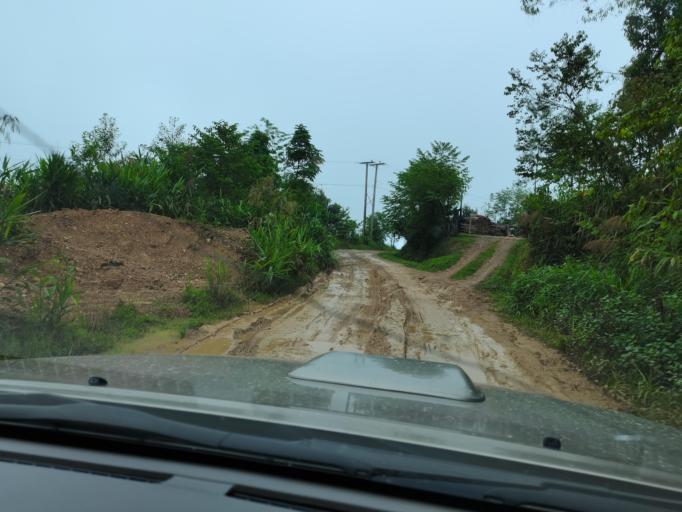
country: LA
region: Phongsali
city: Phongsali
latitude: 21.6457
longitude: 102.0943
